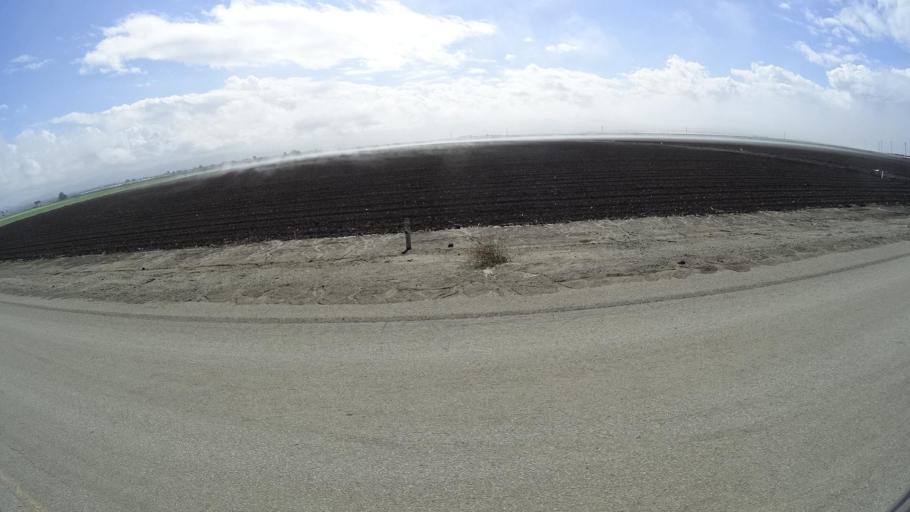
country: US
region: California
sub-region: Monterey County
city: Castroville
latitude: 36.7755
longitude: -121.7879
